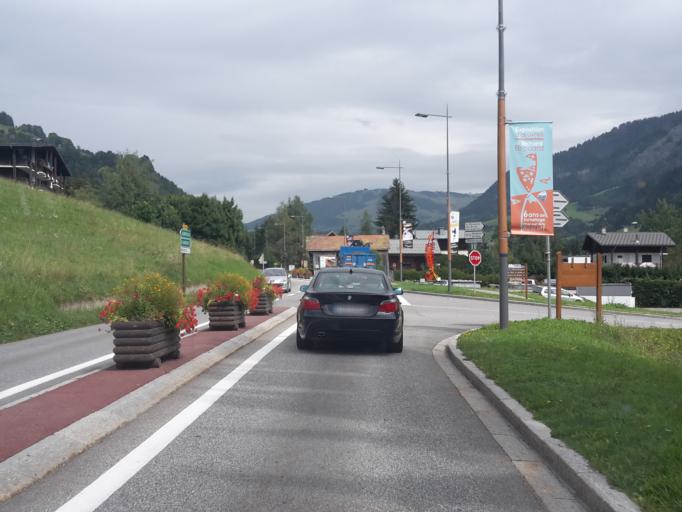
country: FR
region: Rhone-Alpes
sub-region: Departement de la Haute-Savoie
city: Praz-sur-Arly
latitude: 45.8342
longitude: 6.5628
